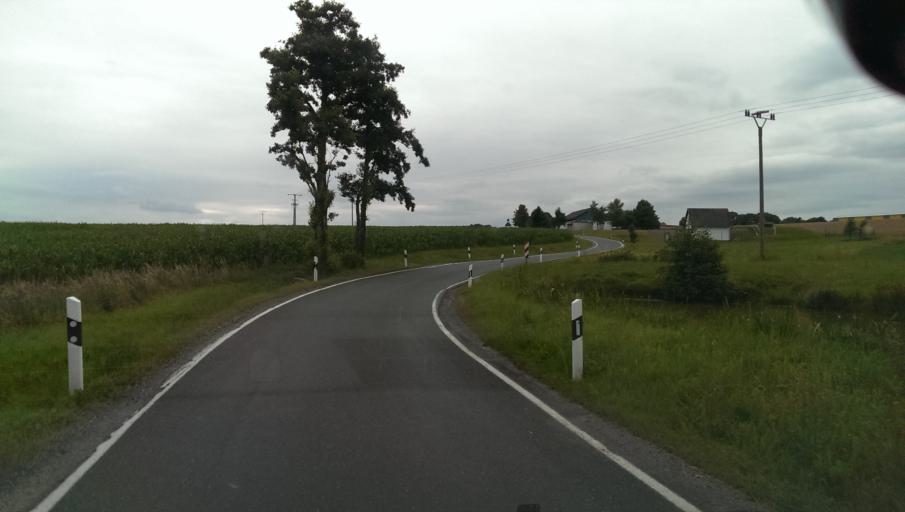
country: DE
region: Thuringia
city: Dittersdorf
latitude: 50.6445
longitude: 11.8282
